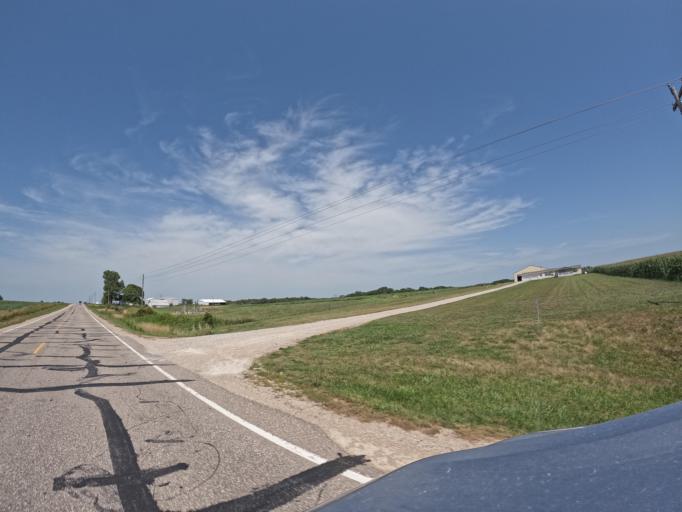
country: US
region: Iowa
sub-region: Henry County
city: Mount Pleasant
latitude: 40.9887
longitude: -91.6122
